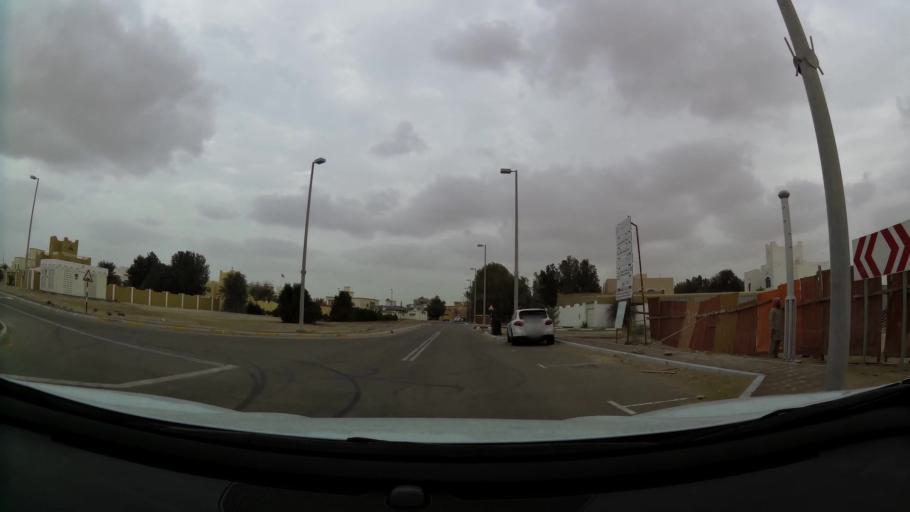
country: AE
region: Abu Dhabi
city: Abu Dhabi
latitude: 24.3842
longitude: 54.6554
